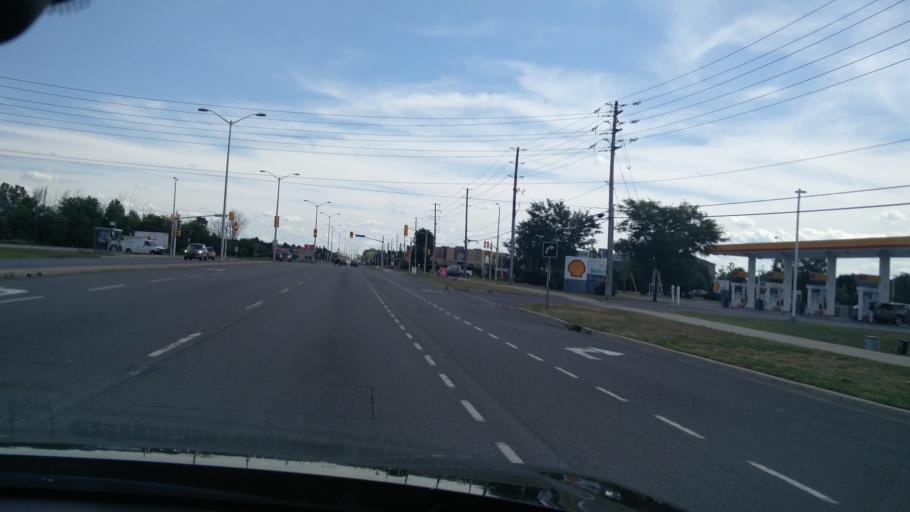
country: CA
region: Ontario
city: Bells Corners
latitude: 45.2924
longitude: -75.7279
